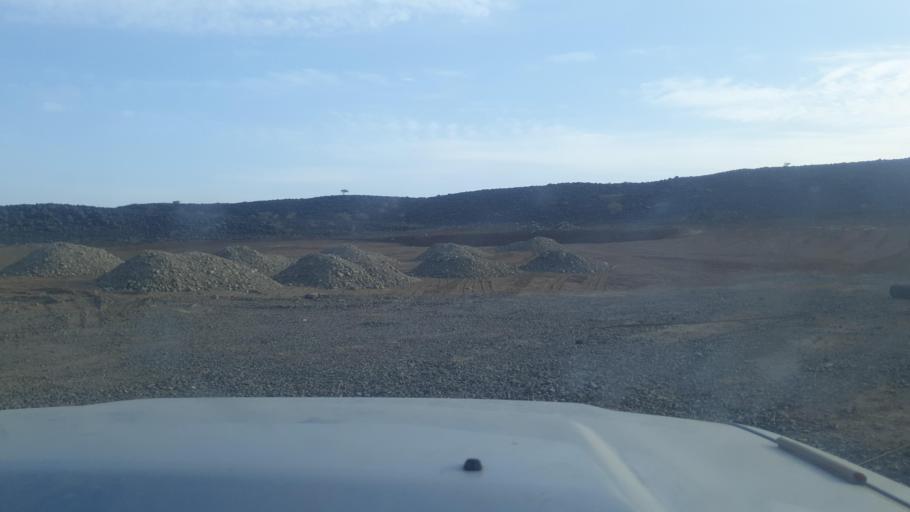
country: DJ
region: Dikhil
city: Dikhil
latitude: 11.1558
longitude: 42.3167
